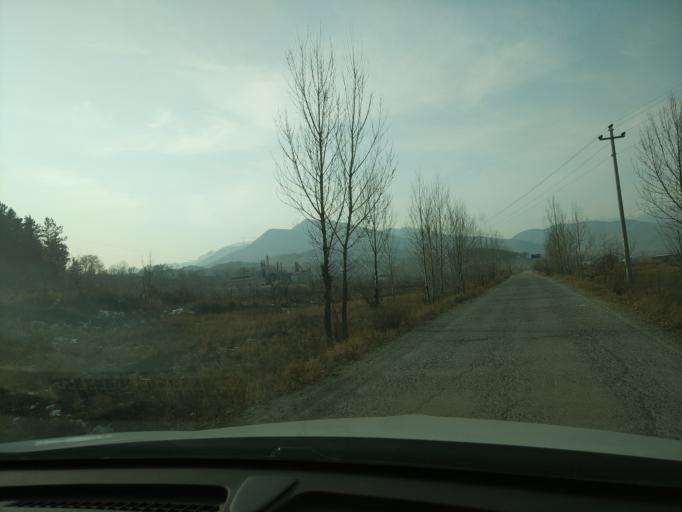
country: CN
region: Hebei
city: Chicheng
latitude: 40.8131
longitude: 115.5410
